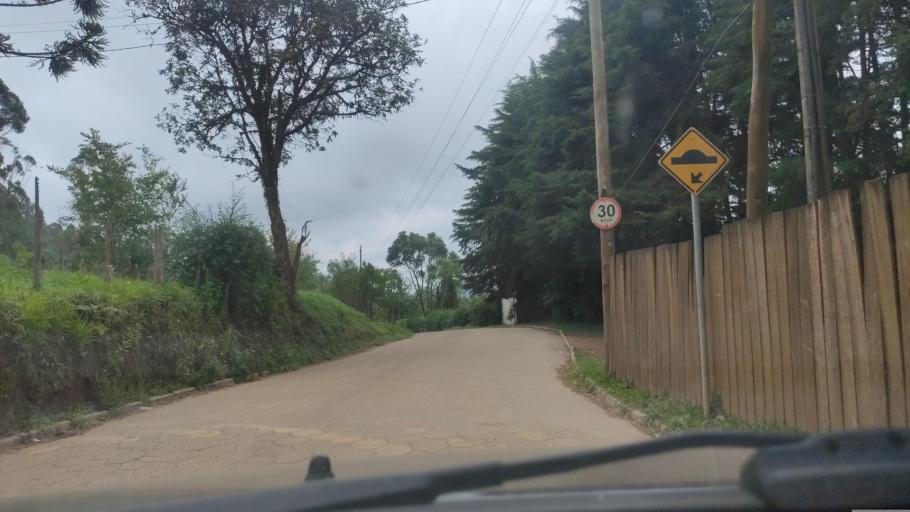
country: BR
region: Minas Gerais
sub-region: Paraisopolis
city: Paraisopolis
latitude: -22.6805
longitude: -45.8532
